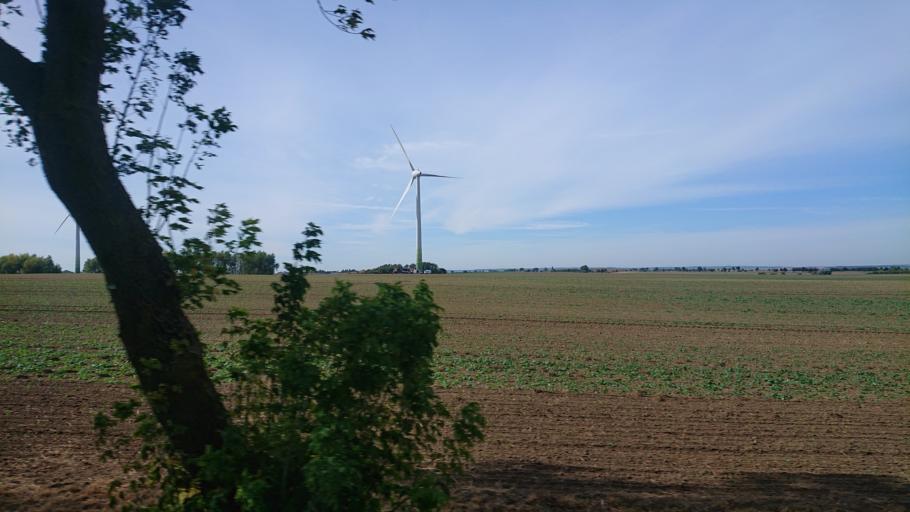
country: DE
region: Brandenburg
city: Grunow
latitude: 53.2597
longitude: 13.9548
